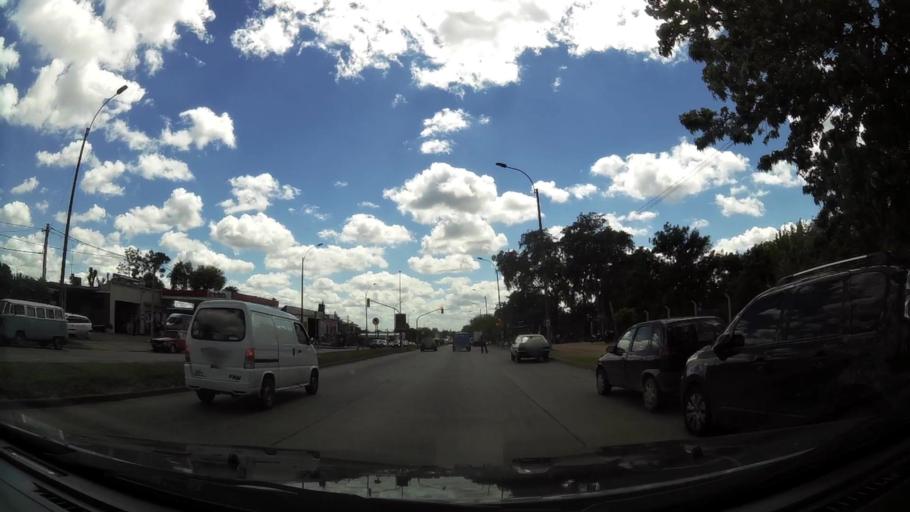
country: UY
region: Canelones
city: Paso de Carrasco
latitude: -34.8382
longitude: -56.1184
